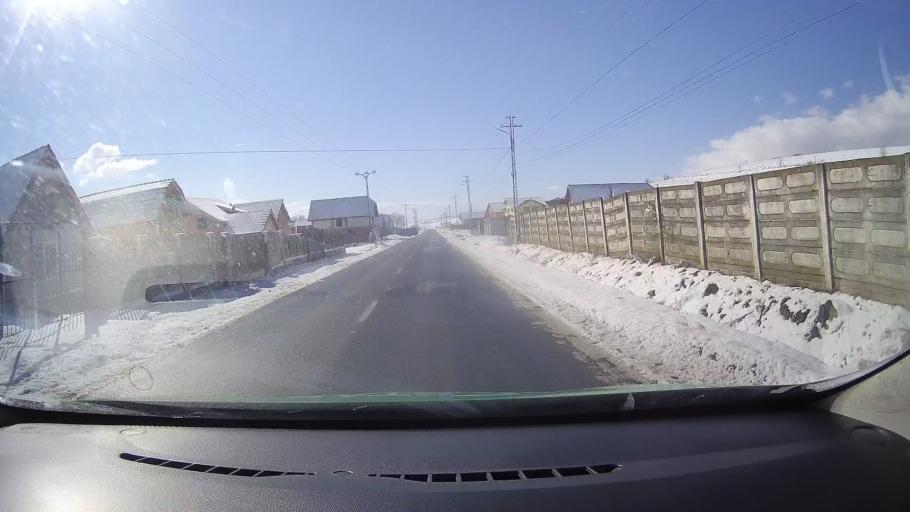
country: RO
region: Sibiu
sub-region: Comuna Vurpar
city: Vurpar
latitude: 45.8883
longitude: 24.3334
